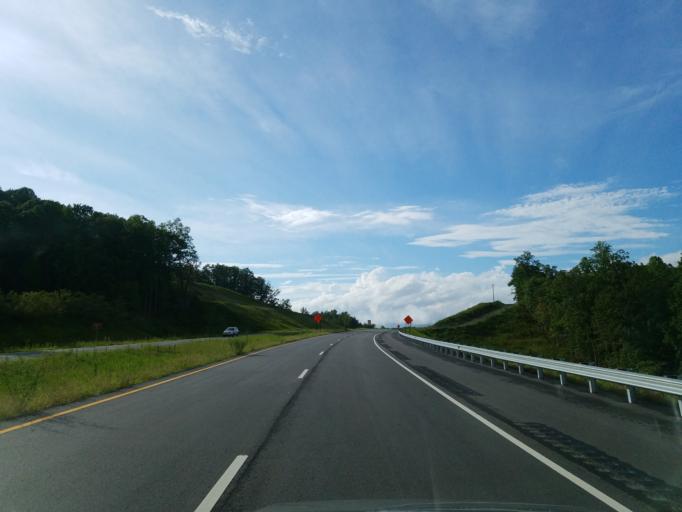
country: US
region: Georgia
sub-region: White County
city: Cleveland
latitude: 34.5846
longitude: -83.7751
